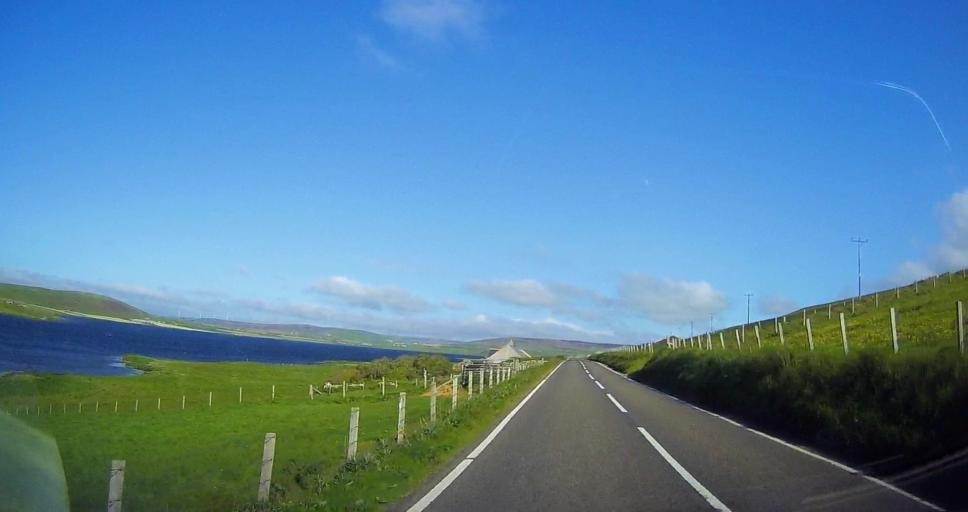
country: GB
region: Scotland
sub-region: Orkney Islands
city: Stromness
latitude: 59.1137
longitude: -3.2977
